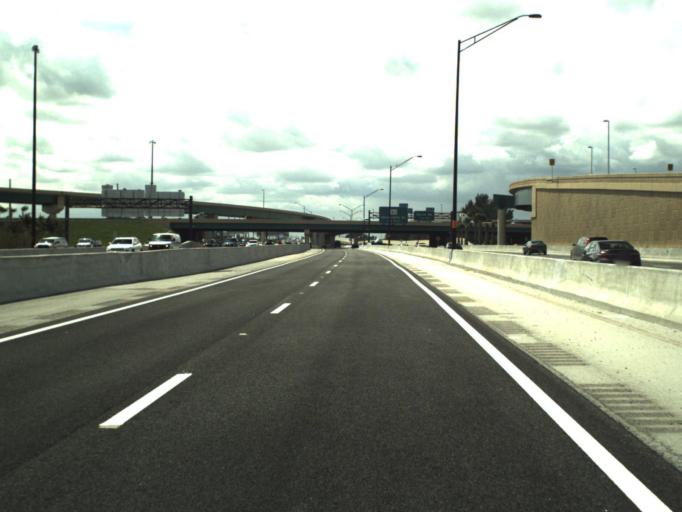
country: US
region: Florida
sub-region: Broward County
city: Broadview Park
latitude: 26.0901
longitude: -80.2137
